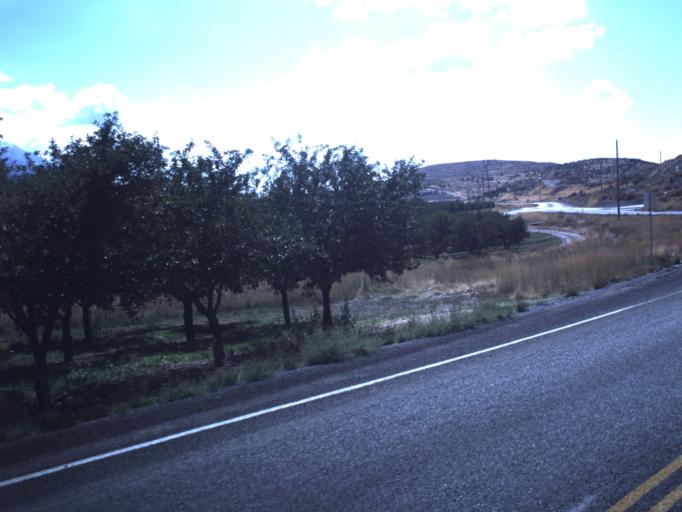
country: US
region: Utah
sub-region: Utah County
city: Santaquin
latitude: 40.0127
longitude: -111.8001
